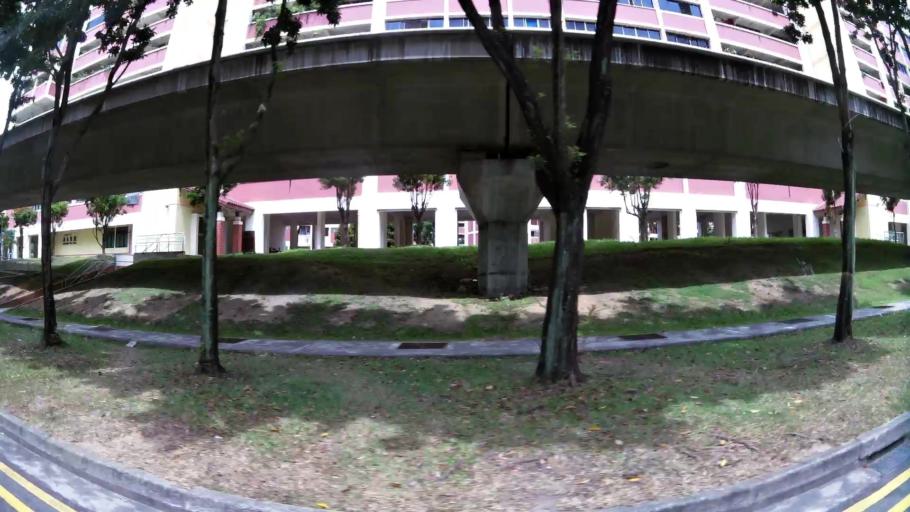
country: MY
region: Johor
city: Johor Bahru
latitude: 1.3782
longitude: 103.7498
